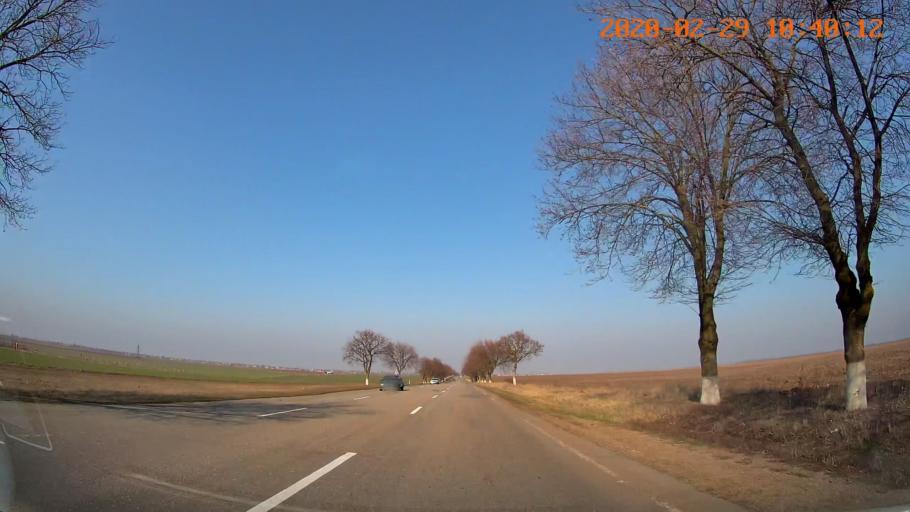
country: MD
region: Anenii Noi
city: Varnita
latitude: 47.0308
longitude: 29.4431
